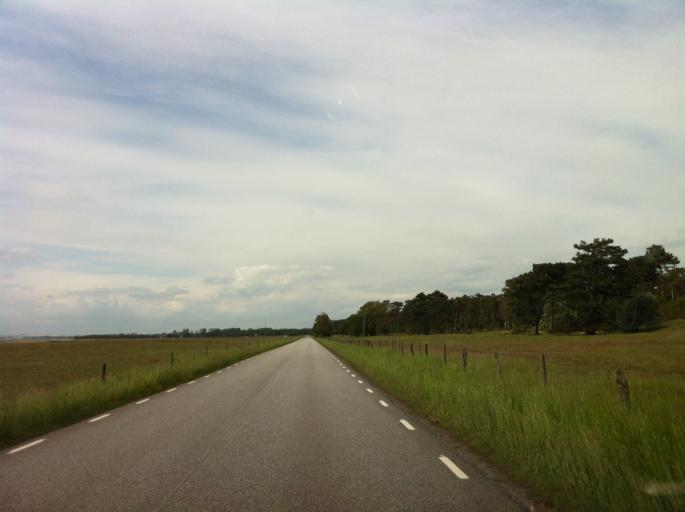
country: SE
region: Skane
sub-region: Kavlinge Kommun
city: Hofterup
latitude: 55.7996
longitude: 12.9376
